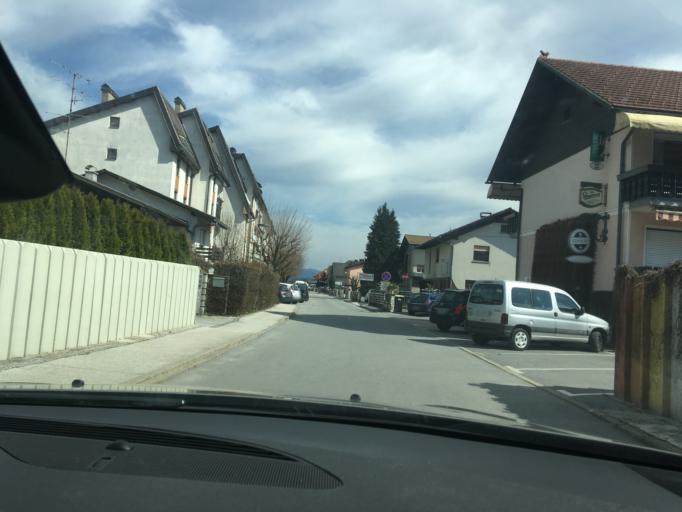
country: SI
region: Menges
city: Menges
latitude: 46.1665
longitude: 14.5736
